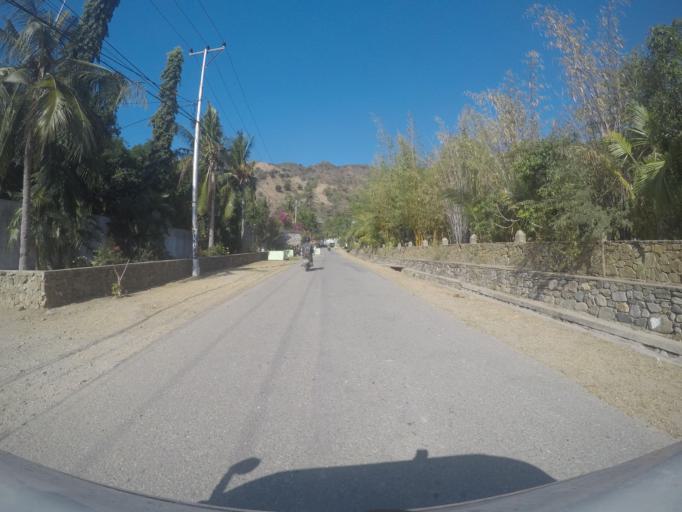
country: TL
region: Dili
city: Dili
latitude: -8.5388
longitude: 125.6157
